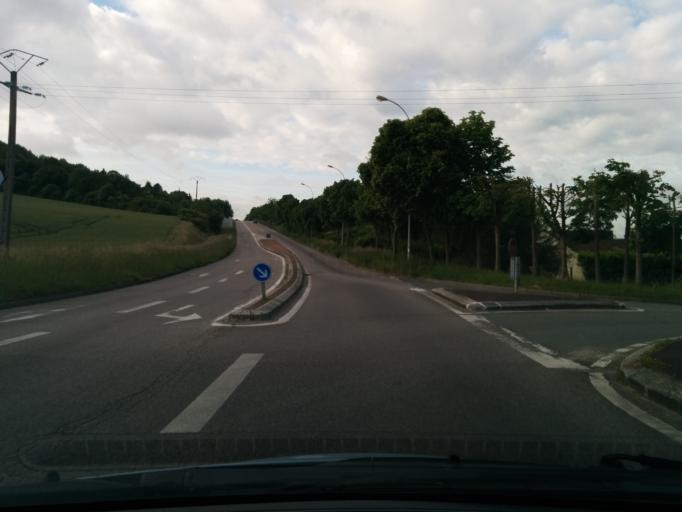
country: FR
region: Ile-de-France
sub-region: Departement des Yvelines
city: Follainville-Dennemont
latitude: 49.0191
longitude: 1.6970
